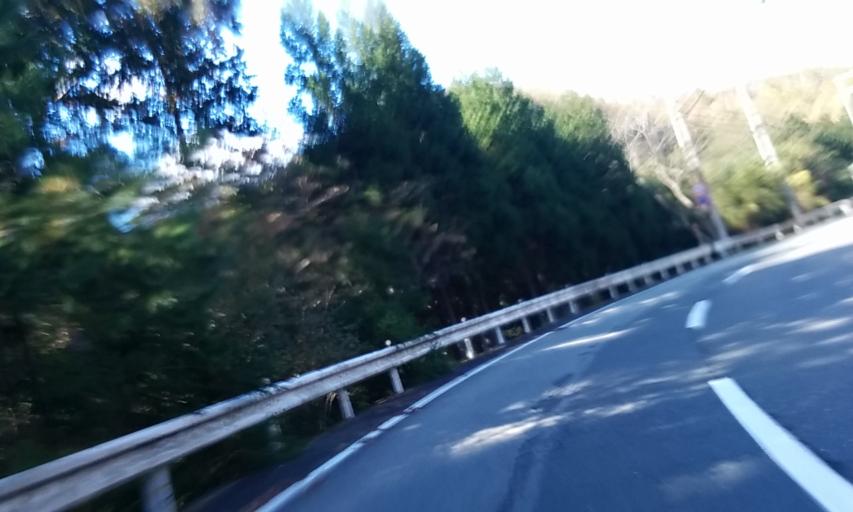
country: JP
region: Kyoto
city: Kameoka
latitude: 35.1990
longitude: 135.6174
